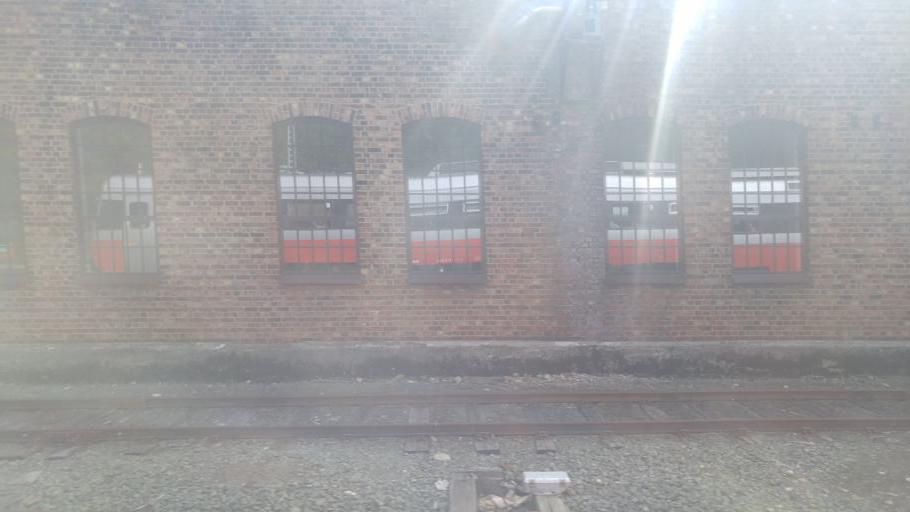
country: NO
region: Sor-Trondelag
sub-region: Midtre Gauldal
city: Storen
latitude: 63.0549
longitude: 10.2867
